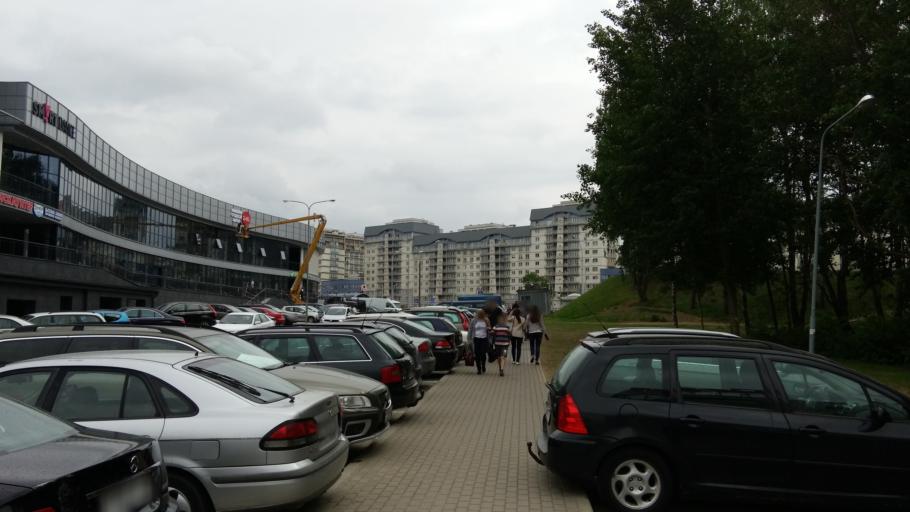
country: BY
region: Minsk
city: Borovlyany
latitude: 53.9463
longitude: 27.6861
